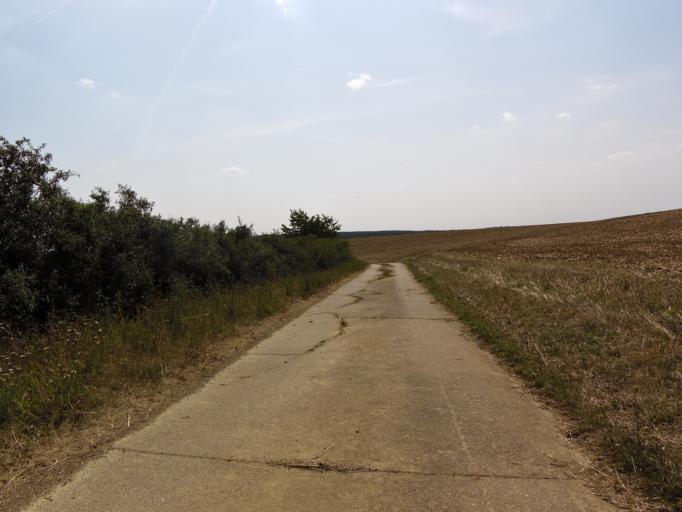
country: DE
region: Bavaria
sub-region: Regierungsbezirk Unterfranken
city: Theilheim
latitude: 49.7654
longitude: 10.0293
